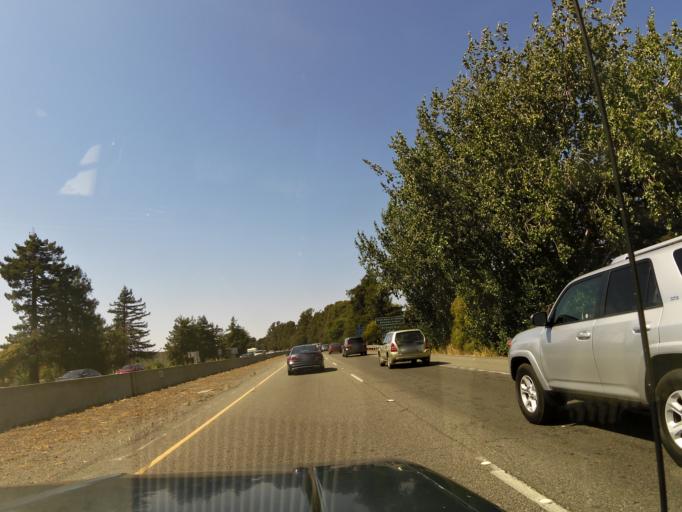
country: US
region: California
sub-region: Sonoma County
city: Petaluma
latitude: 38.2410
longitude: -122.6218
